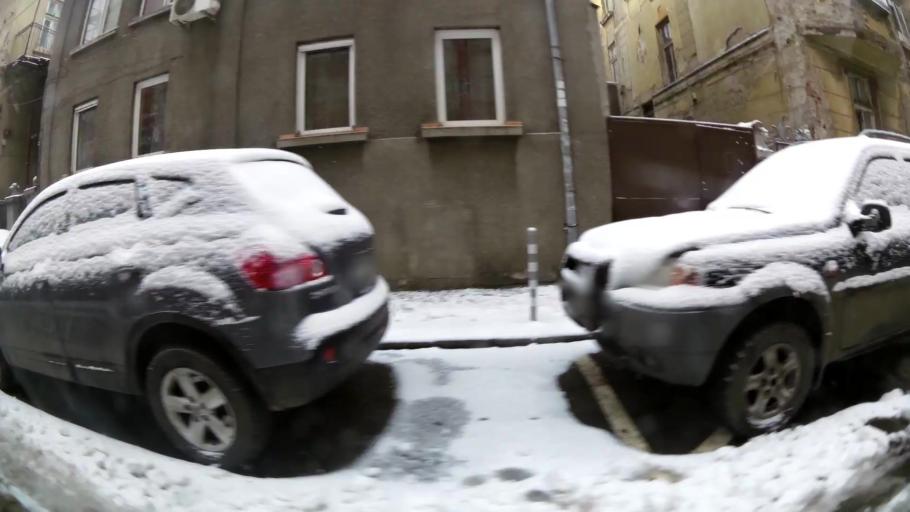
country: BG
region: Sofia-Capital
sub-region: Stolichna Obshtina
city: Sofia
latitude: 42.7033
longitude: 23.3186
